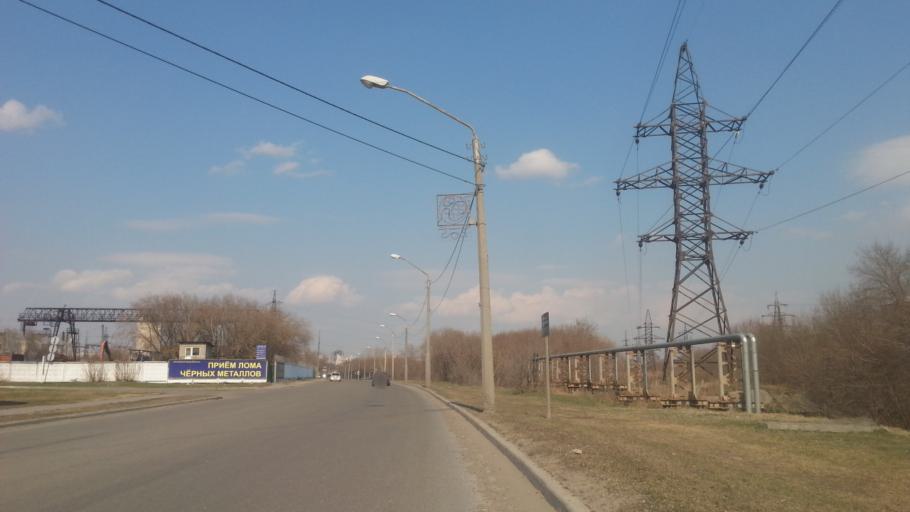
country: RU
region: Altai Krai
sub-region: Gorod Barnaulskiy
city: Barnaul
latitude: 53.3175
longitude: 83.7599
